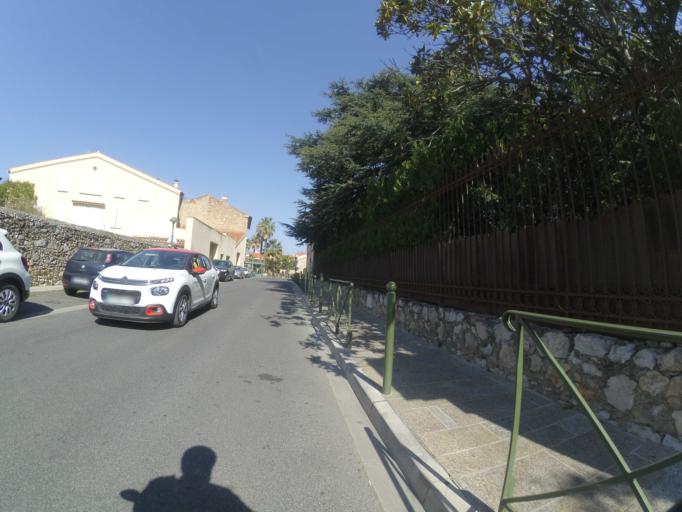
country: FR
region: Languedoc-Roussillon
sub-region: Departement des Pyrenees-Orientales
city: Thuir
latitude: 42.6315
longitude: 2.7570
